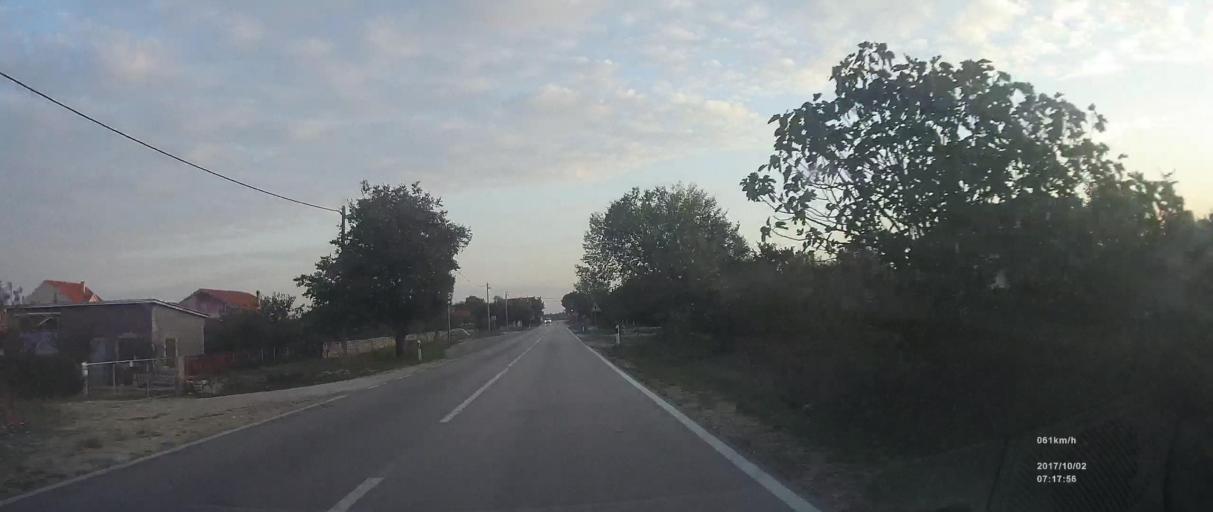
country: HR
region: Zadarska
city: Benkovac
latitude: 44.0139
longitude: 15.5938
